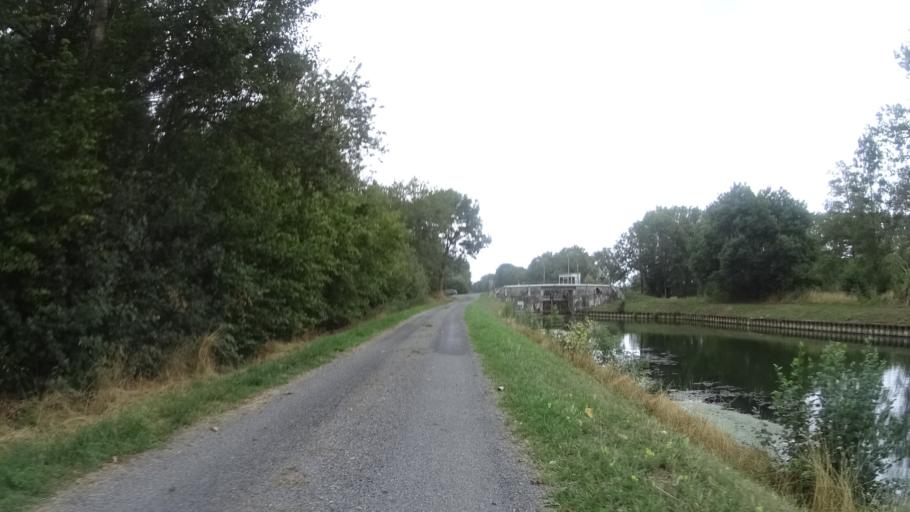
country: FR
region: Picardie
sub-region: Departement de l'Aisne
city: Ribemont
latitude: 49.8241
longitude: 3.4683
